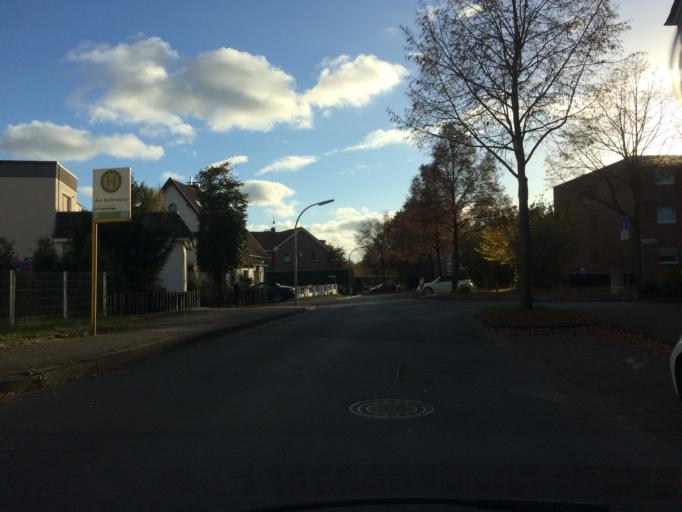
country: DE
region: North Rhine-Westphalia
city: Dorsten
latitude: 51.6690
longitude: 6.9713
